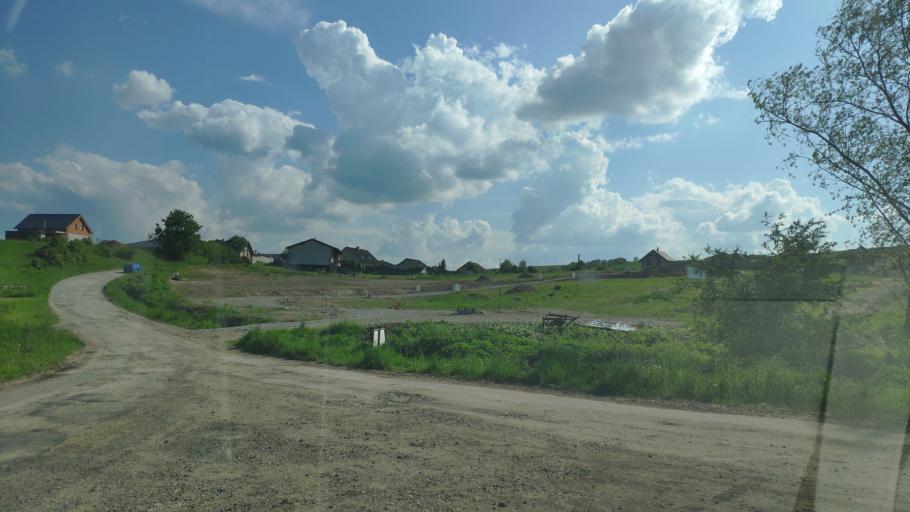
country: SK
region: Presovsky
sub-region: Okres Presov
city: Presov
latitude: 49.0209
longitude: 21.1500
